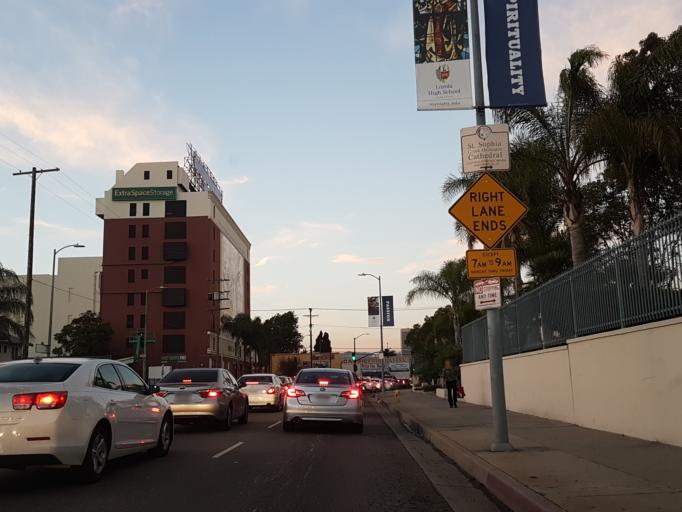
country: US
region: California
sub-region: Los Angeles County
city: Silver Lake
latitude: 34.0458
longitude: -118.3002
